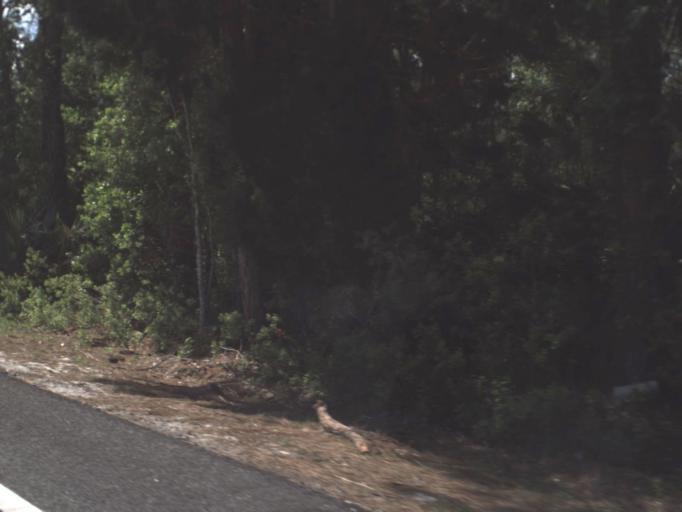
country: US
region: Florida
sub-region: Flagler County
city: Bunnell
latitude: 29.4157
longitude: -81.2077
